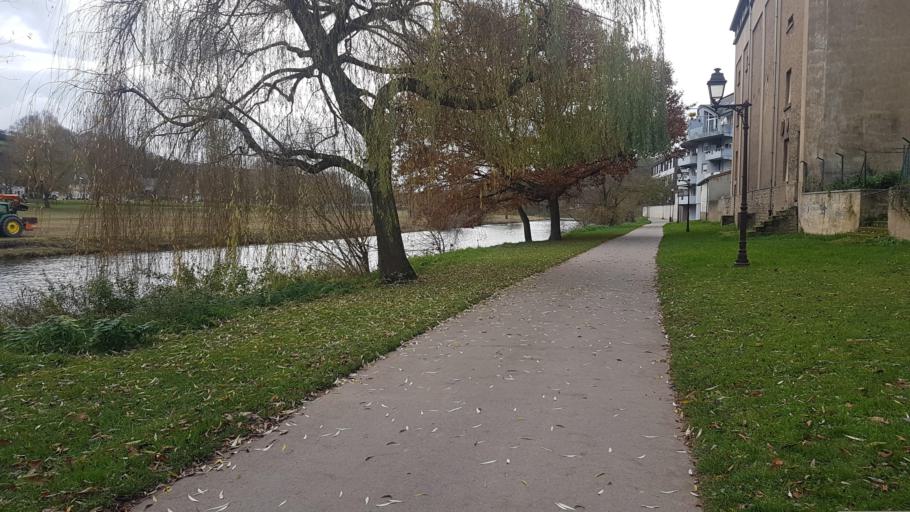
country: LU
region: Diekirch
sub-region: Canton de Diekirch
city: Diekirch
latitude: 49.8644
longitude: 6.1567
